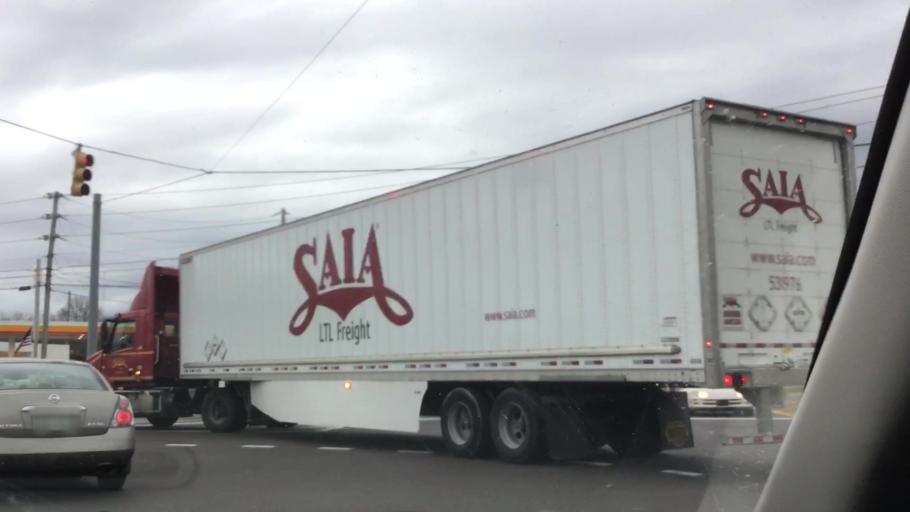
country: US
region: Tennessee
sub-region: Maury County
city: Columbia
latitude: 35.6358
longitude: -87.0176
